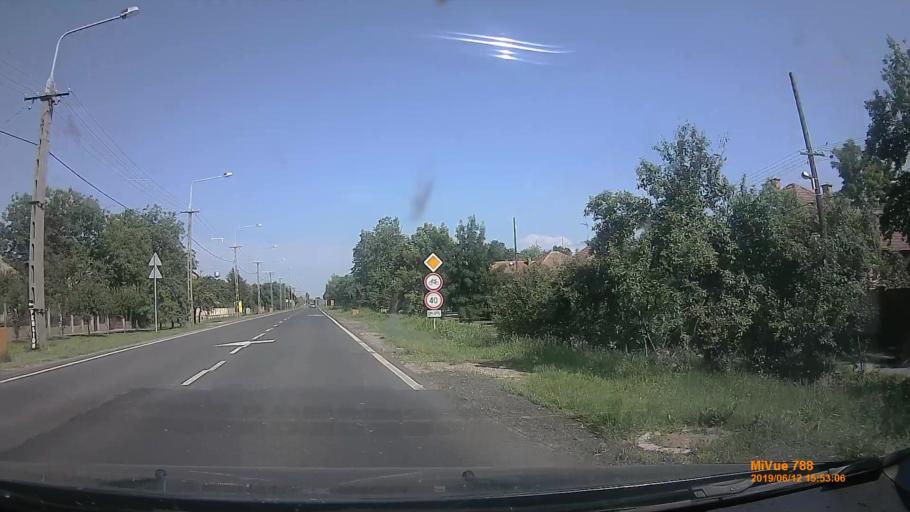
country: HU
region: Csongrad
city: Apatfalva
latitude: 46.1742
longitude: 20.5801
